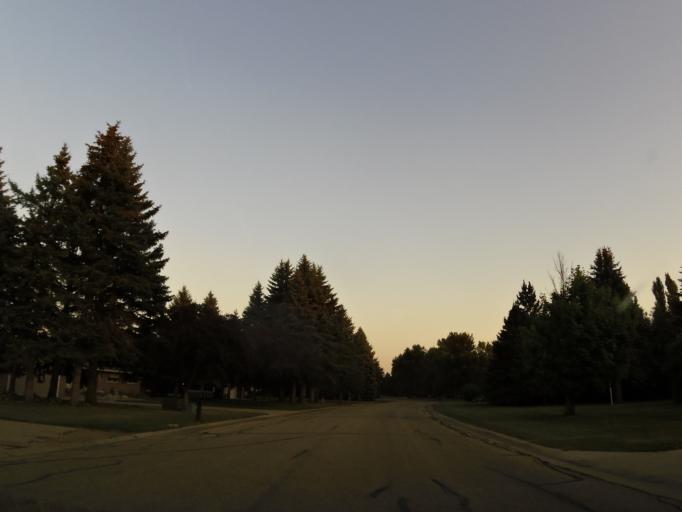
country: US
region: North Dakota
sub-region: Grand Forks County
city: Grand Forks
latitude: 47.8573
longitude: -97.0102
